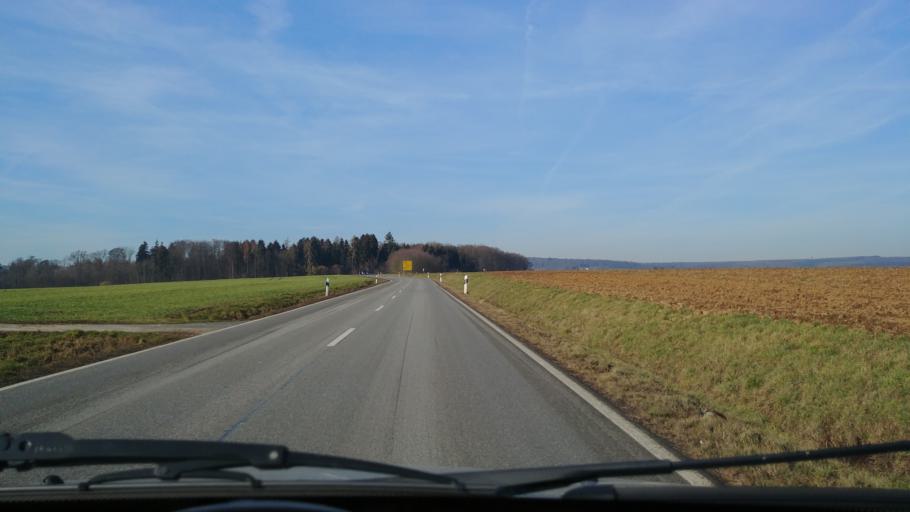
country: DE
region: Rheinland-Pfalz
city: Ehr
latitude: 50.2446
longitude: 7.7864
